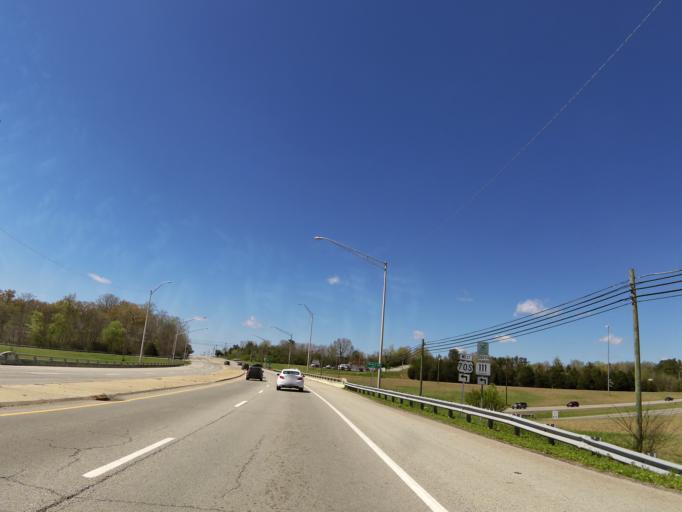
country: US
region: Tennessee
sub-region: White County
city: Sparta
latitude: 35.9362
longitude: -85.4842
